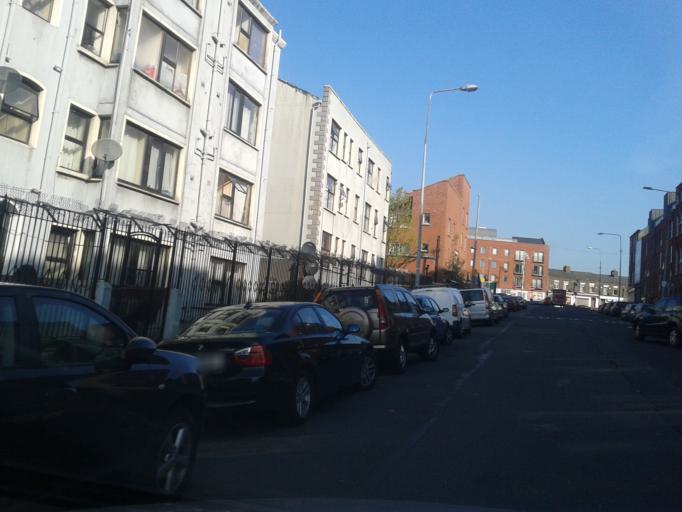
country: IE
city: Fairview
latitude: 53.3553
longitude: -6.2504
